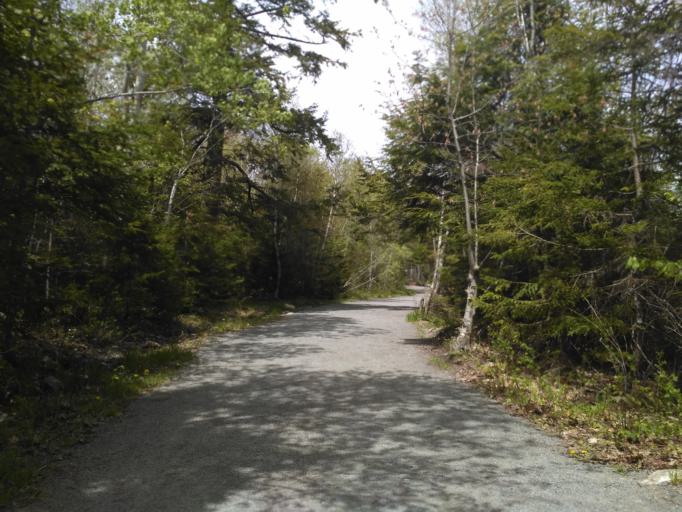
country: CA
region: Nova Scotia
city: Dartmouth
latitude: 44.7744
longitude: -63.6729
